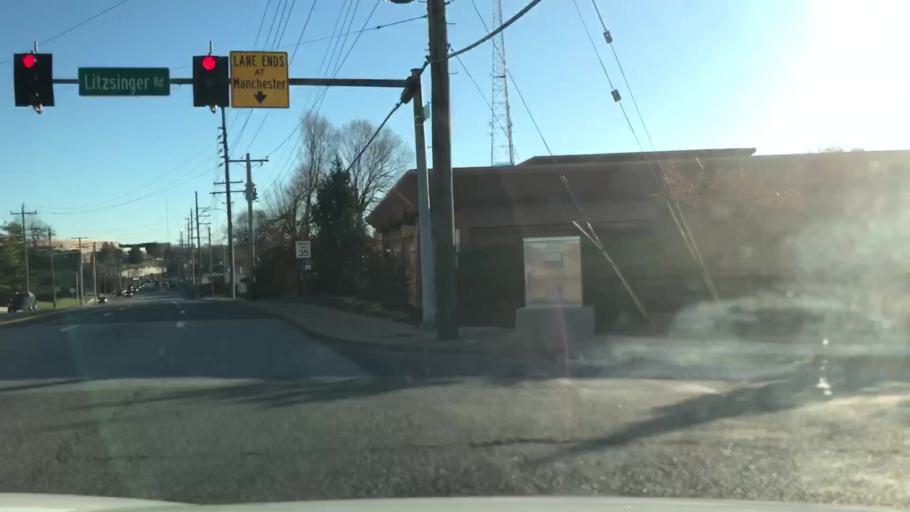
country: US
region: Missouri
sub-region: Saint Louis County
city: Maplewood
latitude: 38.6169
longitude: -90.3346
